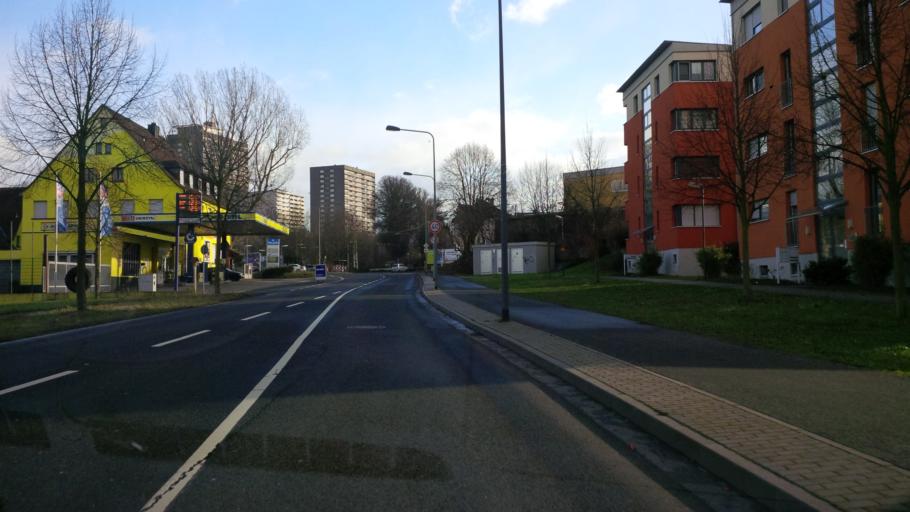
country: DE
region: Hesse
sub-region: Regierungsbezirk Darmstadt
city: Frankfurt am Main
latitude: 50.1714
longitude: 8.6741
